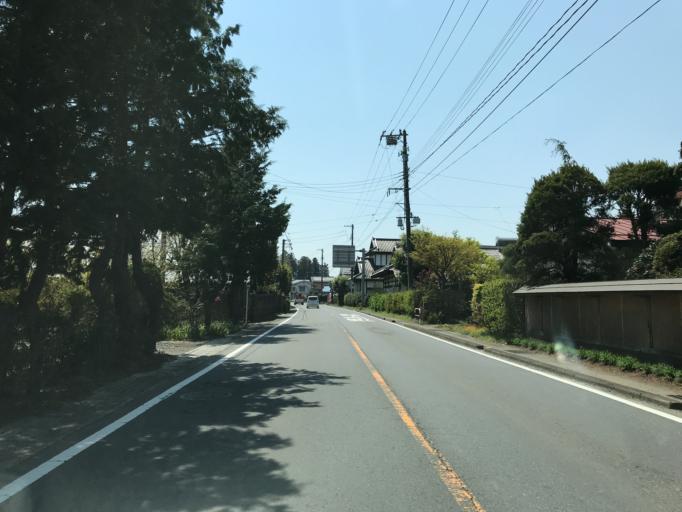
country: JP
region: Fukushima
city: Ishikawa
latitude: 37.1298
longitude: 140.3499
